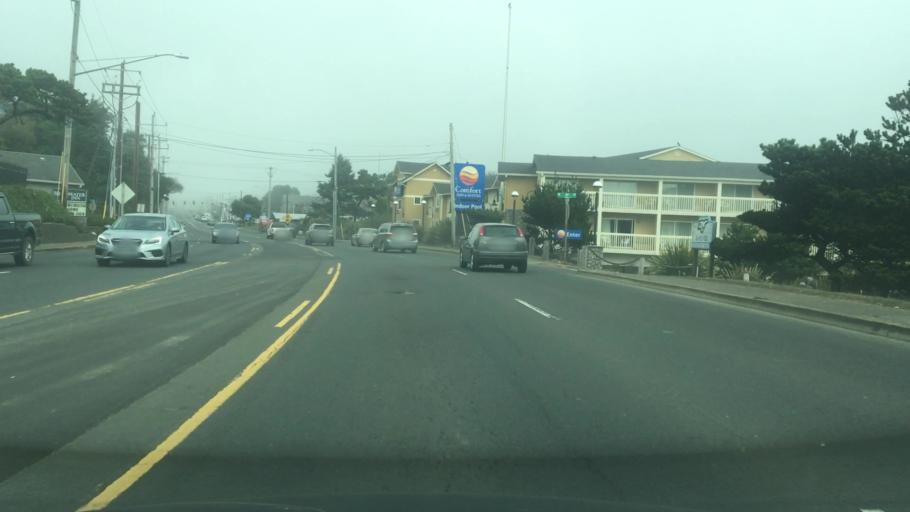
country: US
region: Oregon
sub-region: Lincoln County
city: Lincoln City
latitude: 44.9679
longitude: -124.0158
